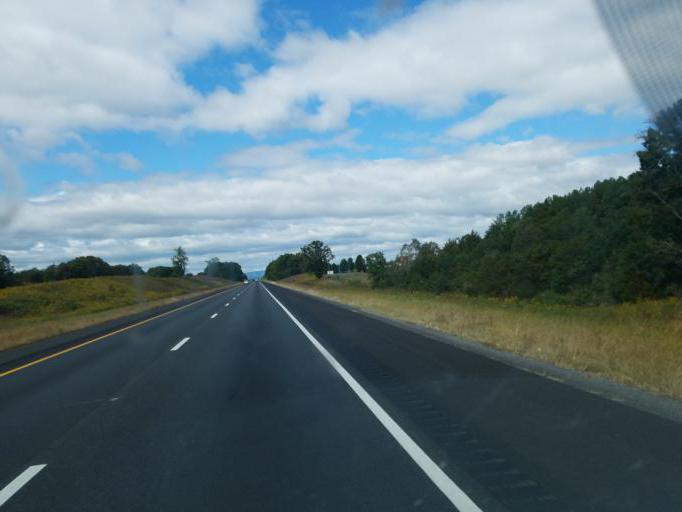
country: US
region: Virginia
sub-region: Warren County
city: Front Royal
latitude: 38.9778
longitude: -78.2209
